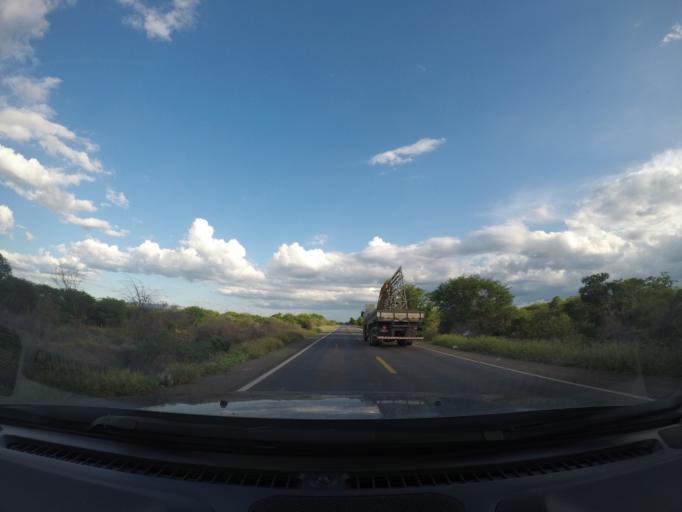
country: BR
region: Bahia
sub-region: Oliveira Dos Brejinhos
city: Beira Rio
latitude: -12.2103
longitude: -42.8028
